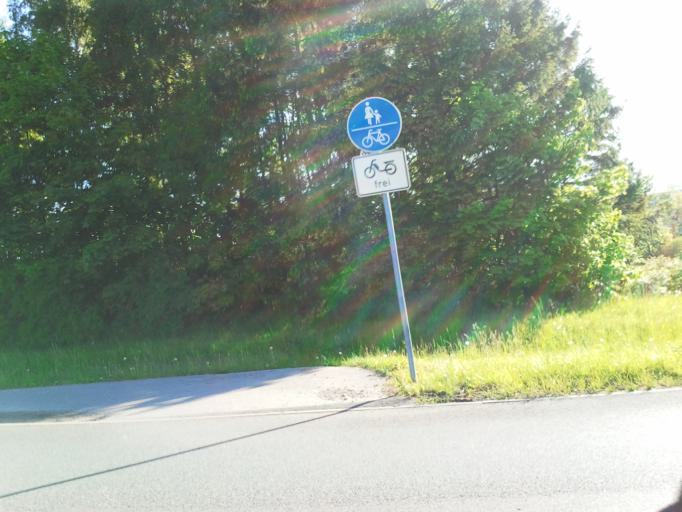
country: DE
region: Mecklenburg-Vorpommern
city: Warnemuende
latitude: 54.1394
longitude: 12.0624
